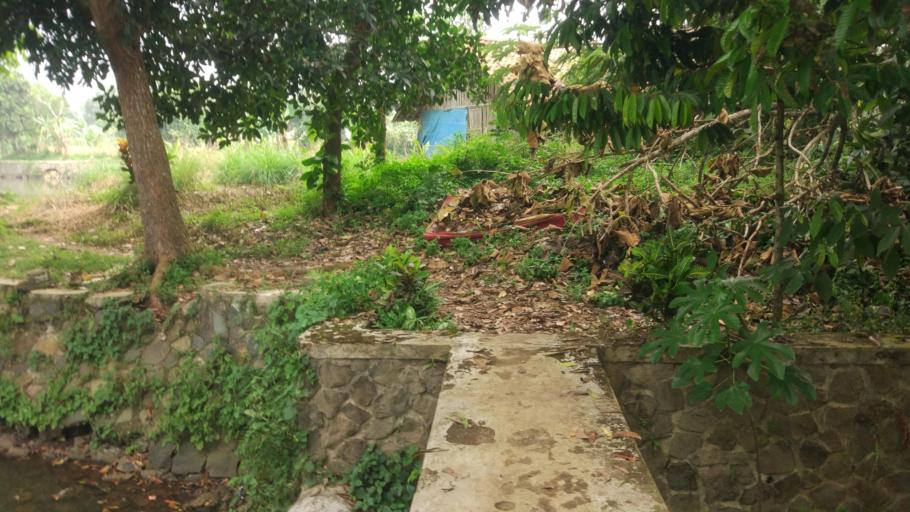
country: ID
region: West Java
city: Ciampea
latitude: -6.5329
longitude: 106.7285
